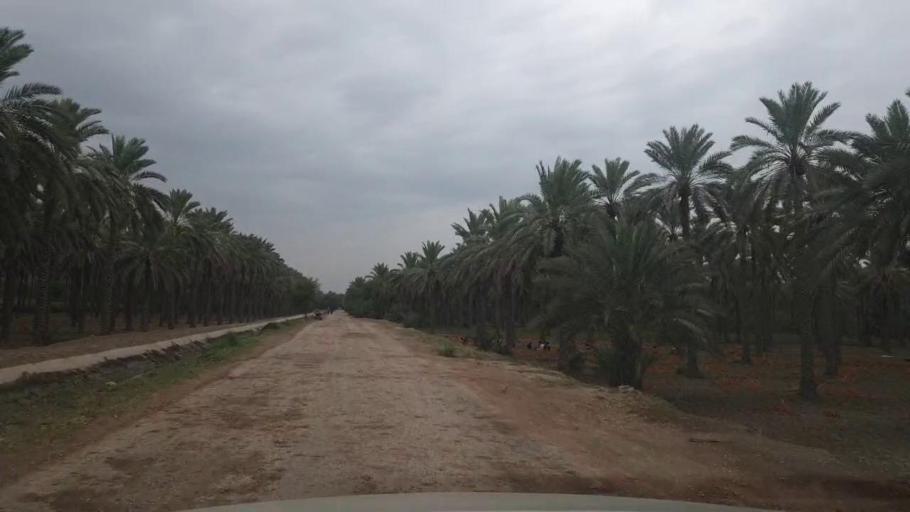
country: PK
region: Sindh
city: Khairpur
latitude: 27.6024
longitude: 68.8157
